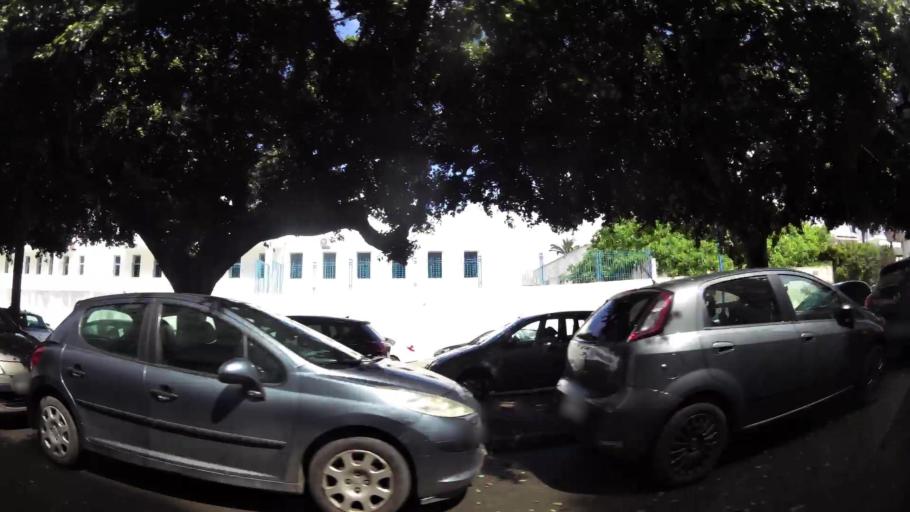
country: MA
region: Grand Casablanca
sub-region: Casablanca
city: Casablanca
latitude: 33.5799
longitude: -7.6215
